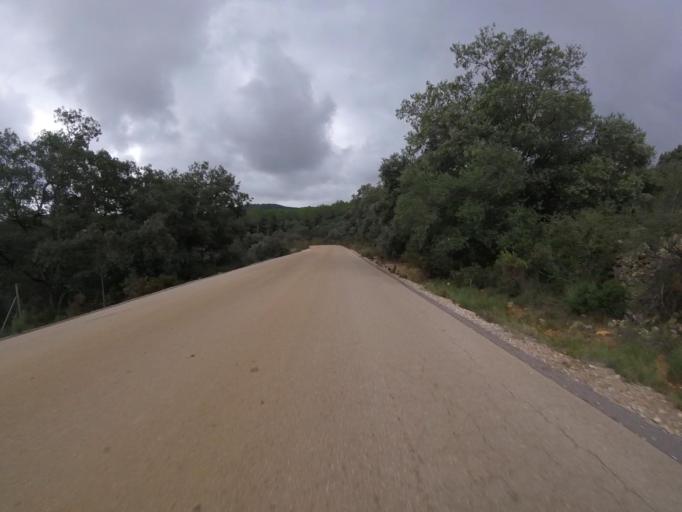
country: ES
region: Valencia
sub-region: Provincia de Castello
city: Benlloch
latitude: 40.2017
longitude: 0.0660
